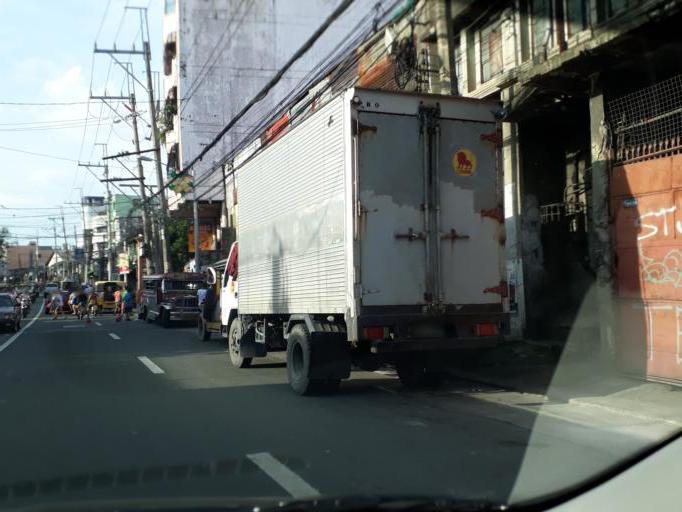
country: PH
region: Metro Manila
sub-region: Caloocan City
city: Niugan
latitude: 14.6400
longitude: 120.9757
